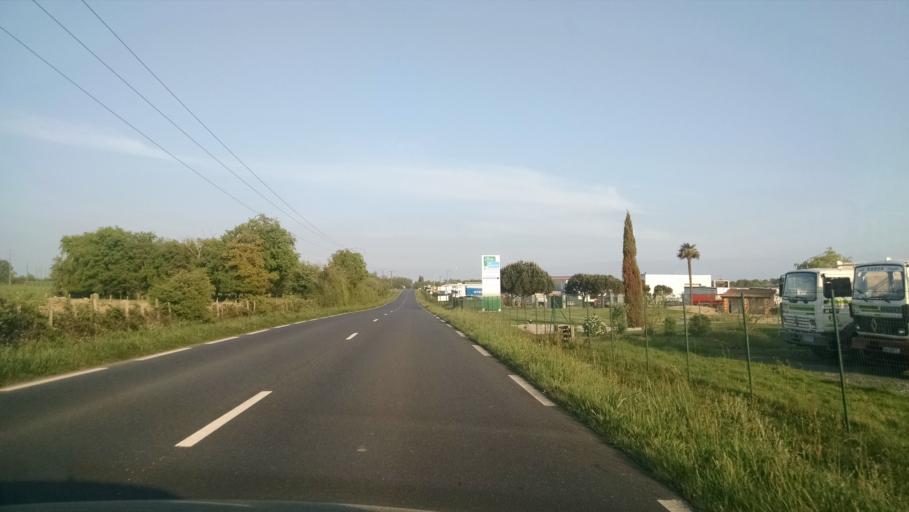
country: FR
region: Pays de la Loire
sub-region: Departement de la Loire-Atlantique
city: Getigne
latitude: 47.0757
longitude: -1.2332
